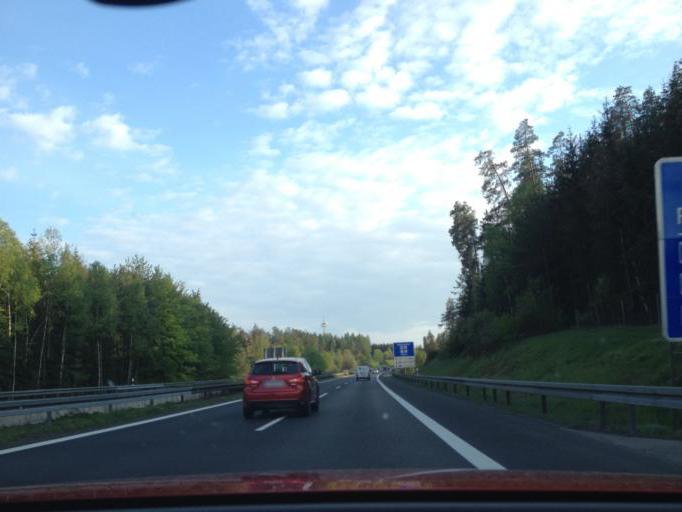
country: DE
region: Bavaria
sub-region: Upper Palatinate
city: Berg
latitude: 49.8523
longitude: 12.1791
